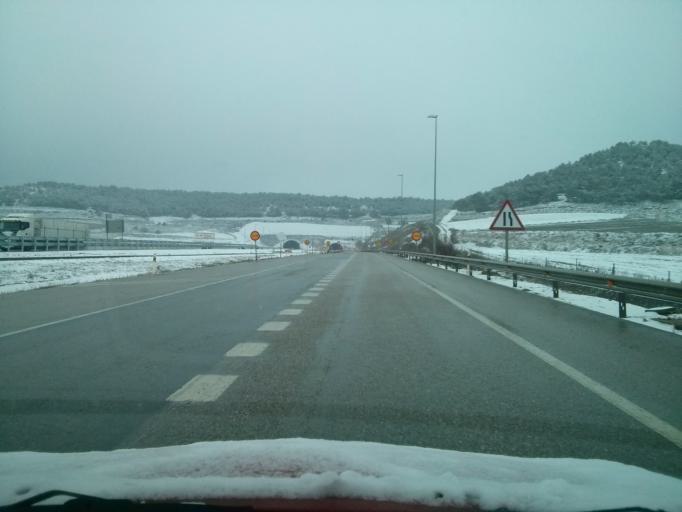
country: ES
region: Castille and Leon
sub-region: Provincia de Burgos
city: Burgos
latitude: 42.3777
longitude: -3.6622
